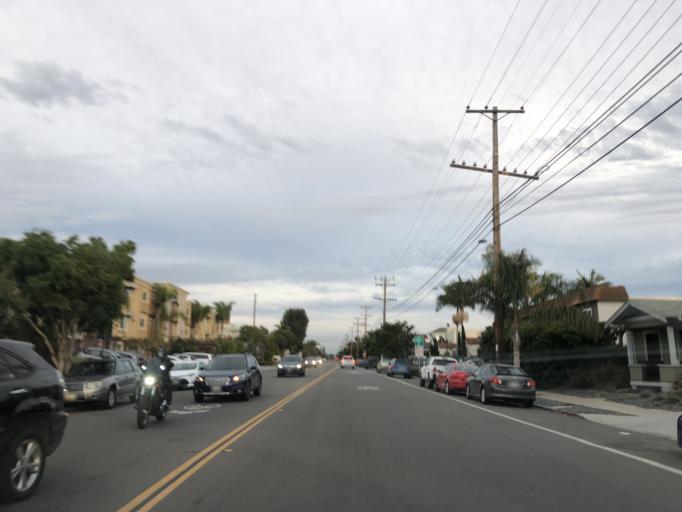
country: US
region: California
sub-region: San Diego County
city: San Diego
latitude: 32.7464
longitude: -117.1551
